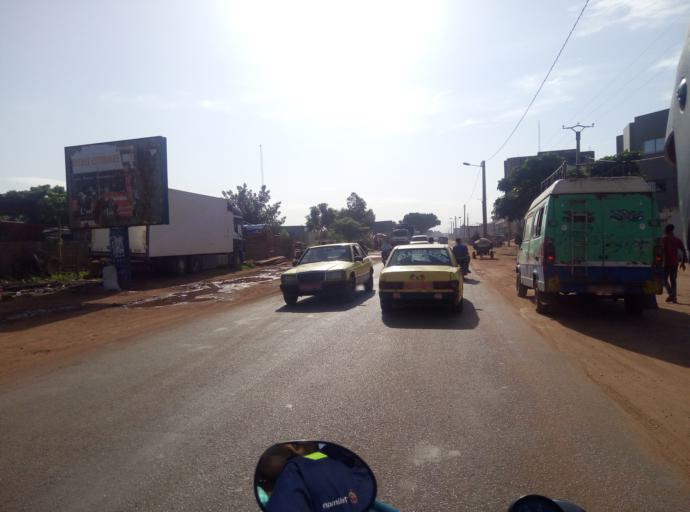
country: ML
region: Bamako
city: Bamako
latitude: 12.6525
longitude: -7.9441
